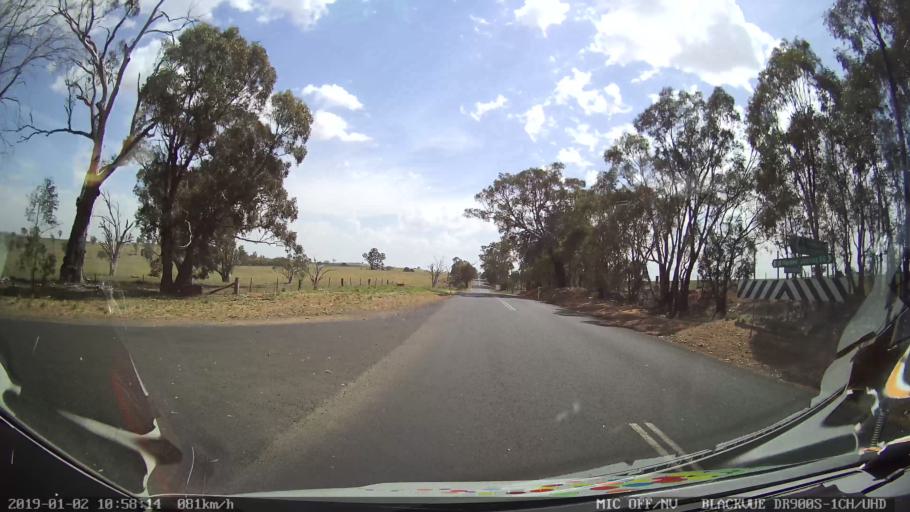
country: AU
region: New South Wales
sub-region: Cootamundra
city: Cootamundra
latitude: -34.6265
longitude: 148.2893
